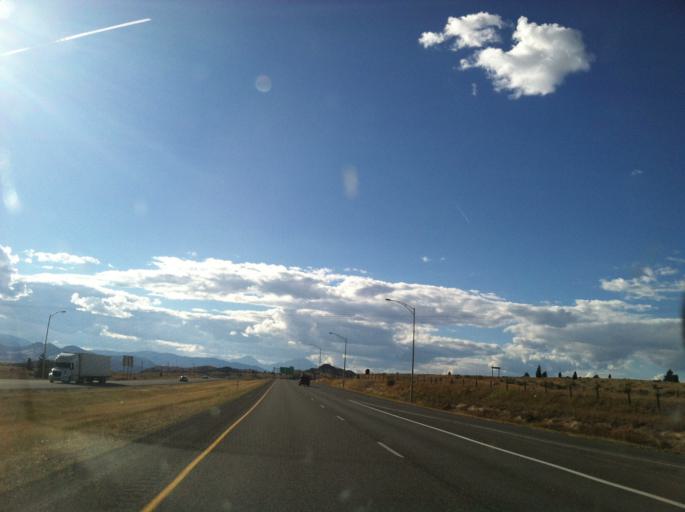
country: US
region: Montana
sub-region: Silver Bow County
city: Butte
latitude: 46.0076
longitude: -112.6172
